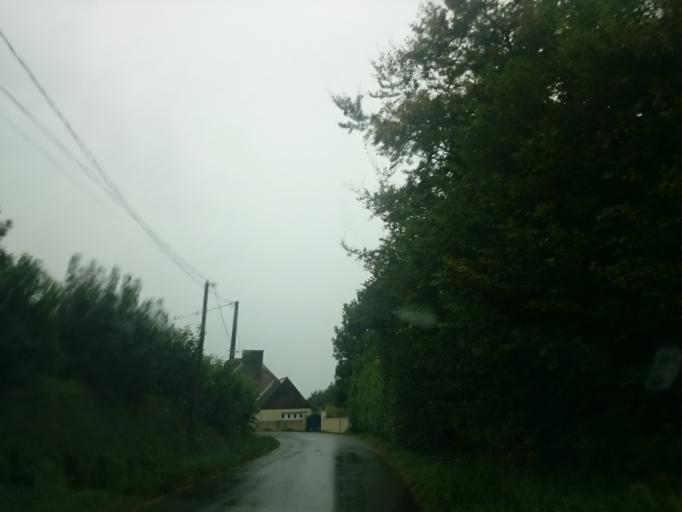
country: FR
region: Brittany
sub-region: Departement du Finistere
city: Kernilis
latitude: 48.5554
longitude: -4.4000
